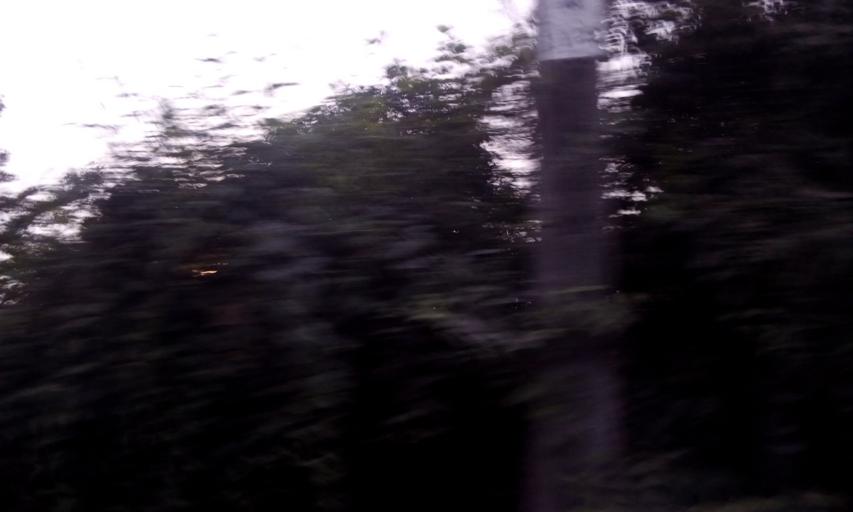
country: TH
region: Bangkok
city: Nong Chok
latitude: 13.8508
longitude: 100.8853
